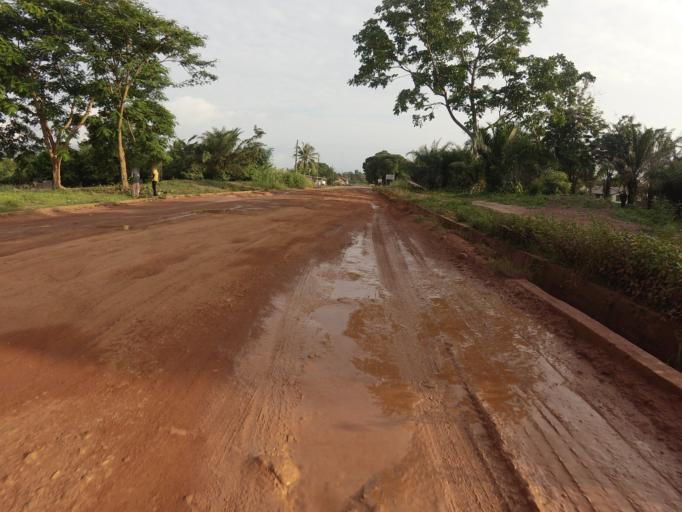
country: GH
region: Volta
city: Kpandu
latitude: 6.9598
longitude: 0.4594
